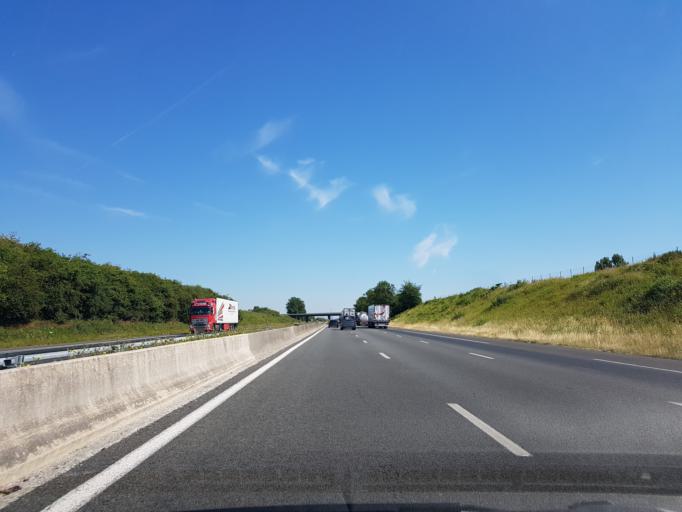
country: FR
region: Picardie
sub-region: Departement de l'Oise
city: Ressons-sur-Matz
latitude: 49.5099
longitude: 2.7187
